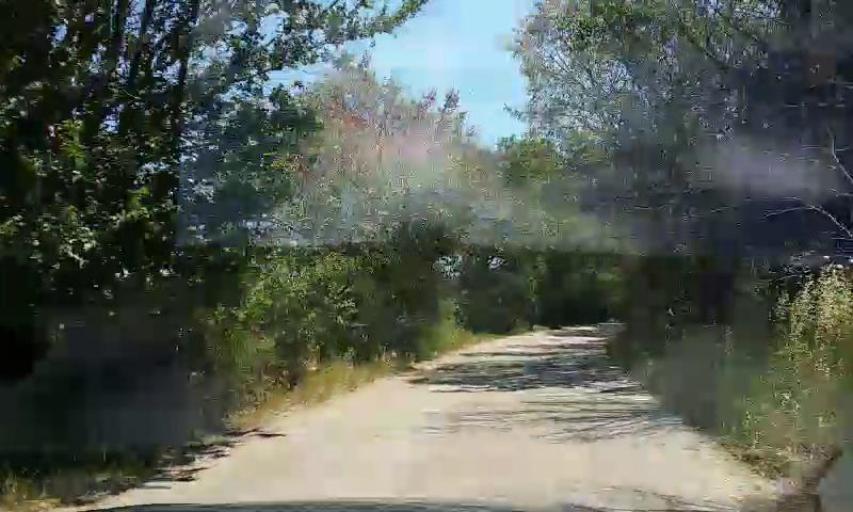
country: IT
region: Molise
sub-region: Provincia di Campobasso
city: Guglionesi
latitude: 41.9373
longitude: 14.8891
